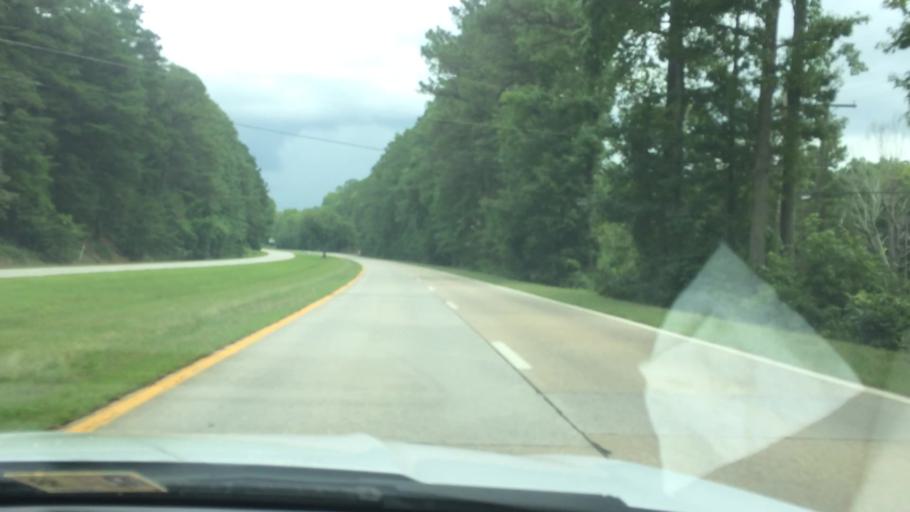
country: US
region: Virginia
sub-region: King William County
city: West Point
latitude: 37.4069
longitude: -76.8531
